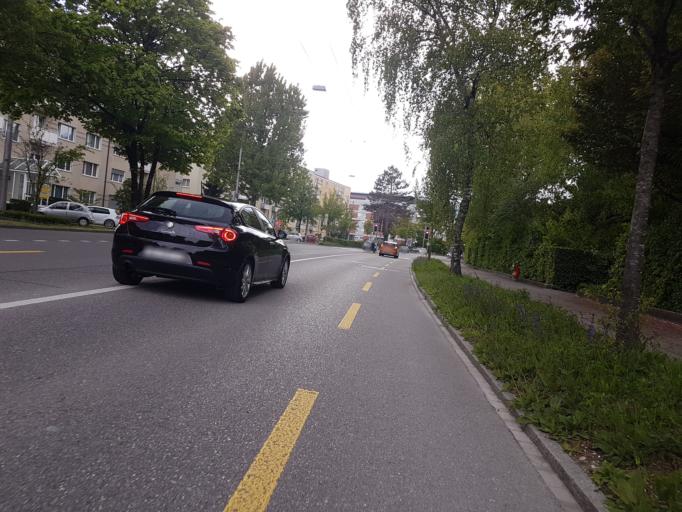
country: CH
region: Bern
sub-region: Biel/Bienne District
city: Brugg
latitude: 47.1428
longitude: 7.2798
